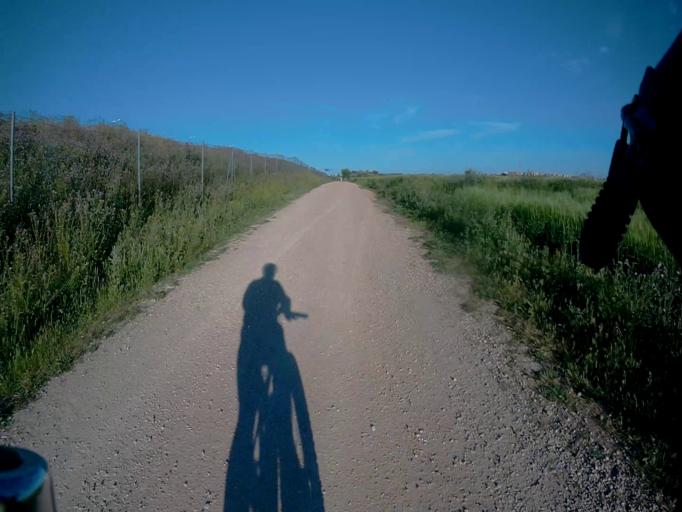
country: ES
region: Madrid
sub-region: Provincia de Madrid
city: Alcorcon
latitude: 40.3208
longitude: -3.8299
